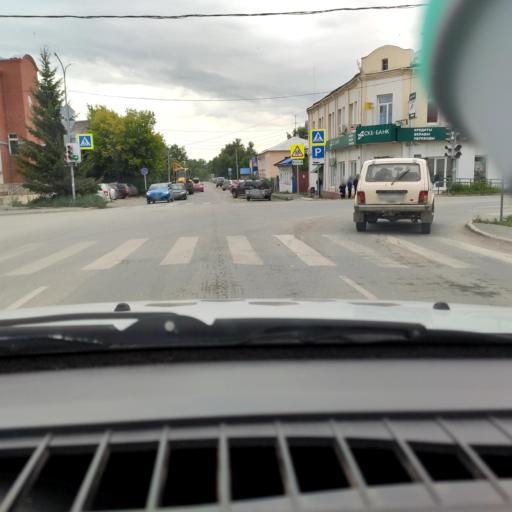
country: RU
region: Sverdlovsk
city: Krasnoufimsk
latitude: 56.6200
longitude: 57.7728
